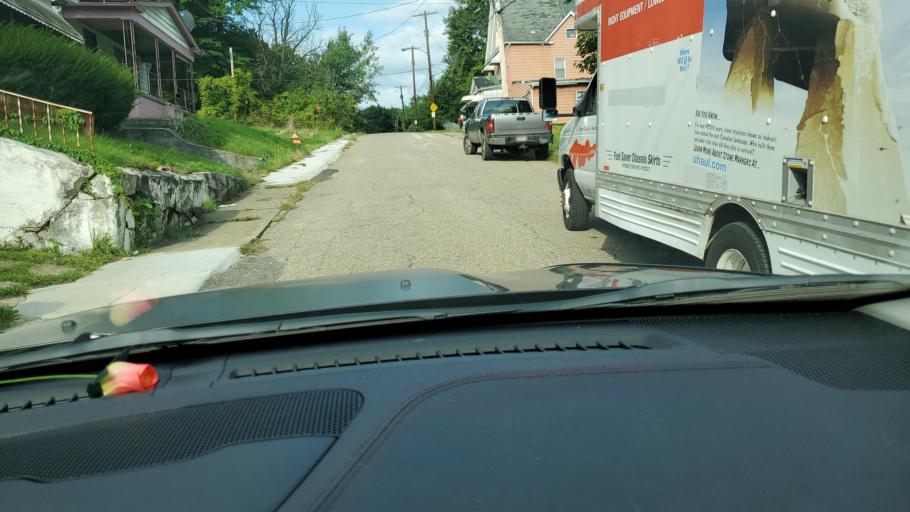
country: US
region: Ohio
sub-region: Mahoning County
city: Youngstown
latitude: 41.0952
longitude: -80.6609
